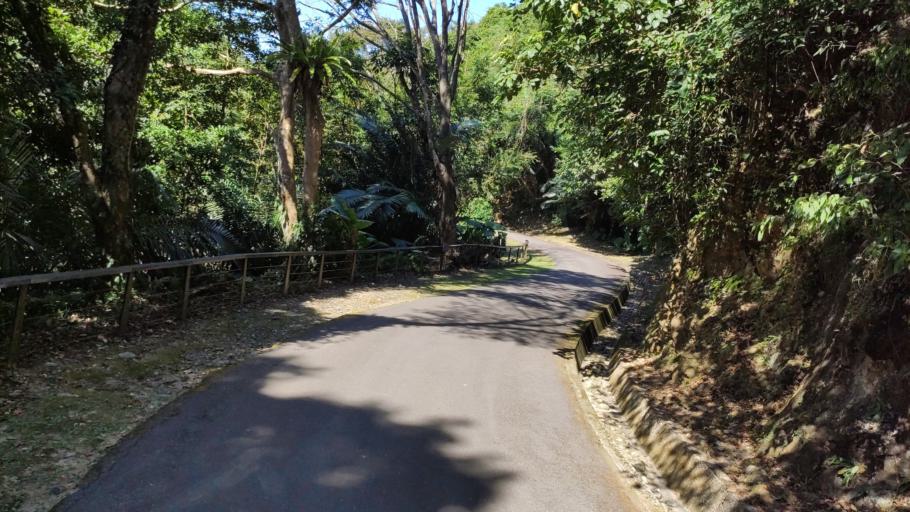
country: TW
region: Taiwan
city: Daxi
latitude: 24.8410
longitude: 121.3059
